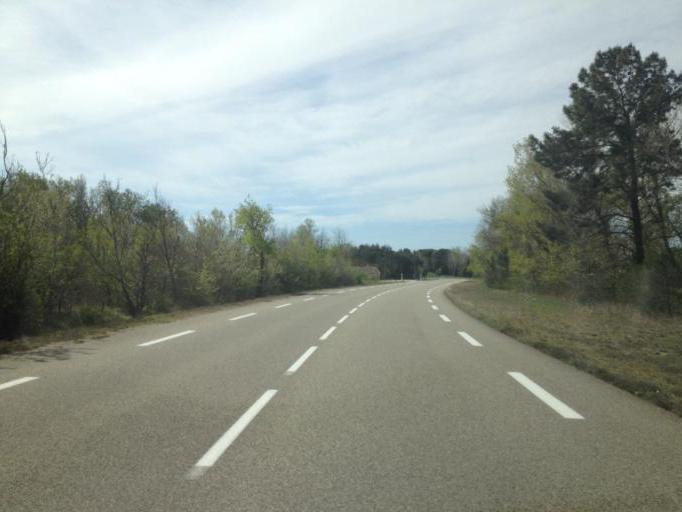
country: FR
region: Provence-Alpes-Cote d'Azur
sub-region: Departement du Vaucluse
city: Caderousse
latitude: 44.1031
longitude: 4.7295
